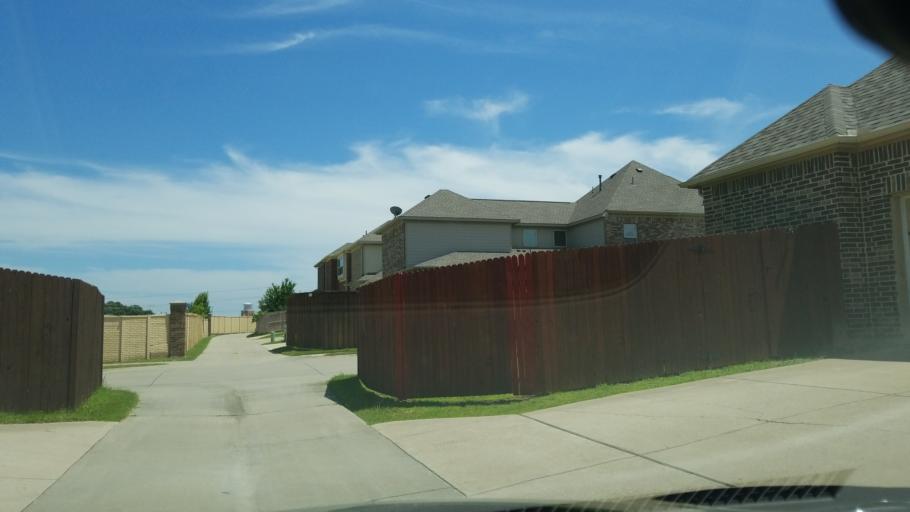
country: US
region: Texas
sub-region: Dallas County
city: Irving
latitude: 32.8766
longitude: -96.9951
